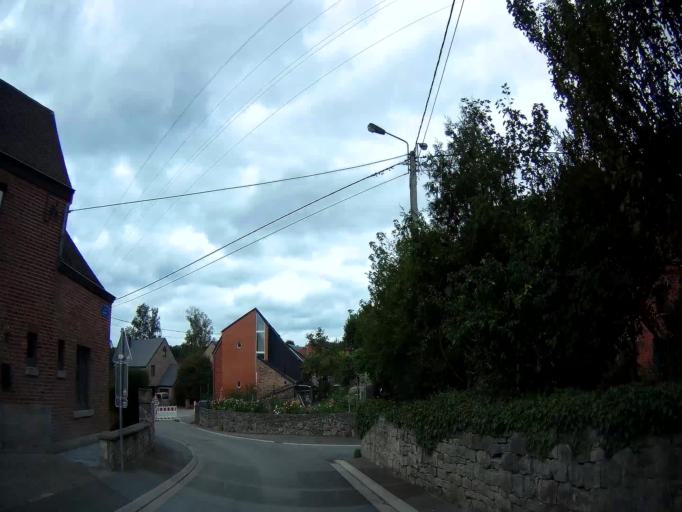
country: BE
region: Wallonia
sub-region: Province de Namur
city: Rochefort
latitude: 50.1635
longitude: 5.2271
